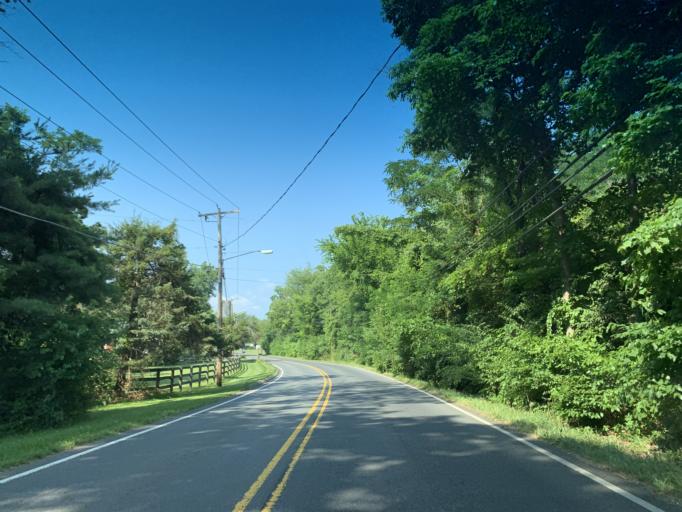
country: US
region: Maryland
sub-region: Montgomery County
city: Poolesville
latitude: 39.1752
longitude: -77.4148
